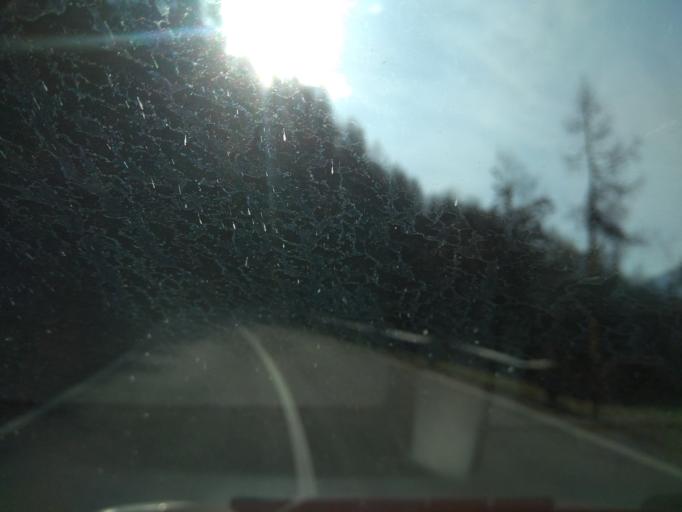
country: IT
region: Trentino-Alto Adige
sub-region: Provincia di Trento
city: Sover
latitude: 46.2202
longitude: 11.3181
